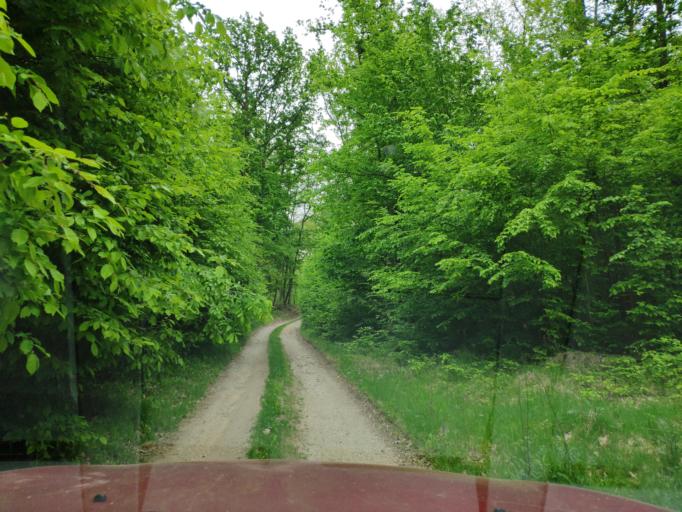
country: HU
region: Borsod-Abauj-Zemplen
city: Putnok
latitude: 48.4966
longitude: 20.3078
